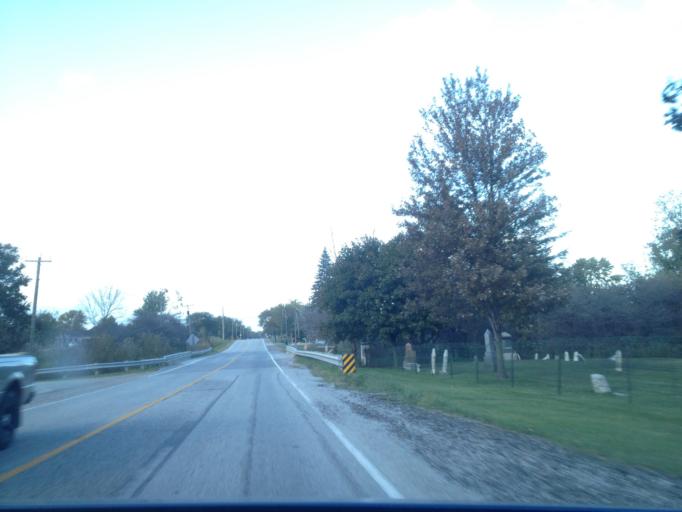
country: US
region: Michigan
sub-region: Wayne County
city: Grosse Pointe
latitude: 42.1769
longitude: -82.7203
